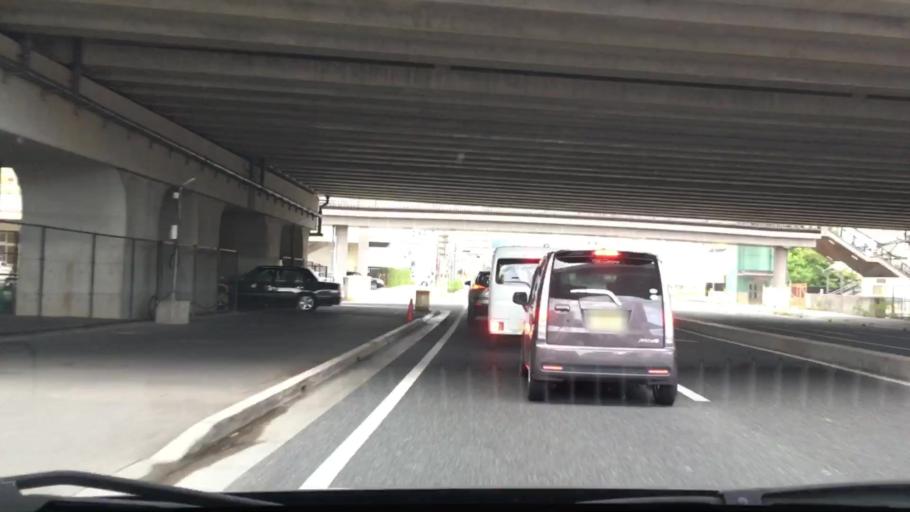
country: JP
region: Hyogo
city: Himeji
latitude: 34.8259
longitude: 134.6954
